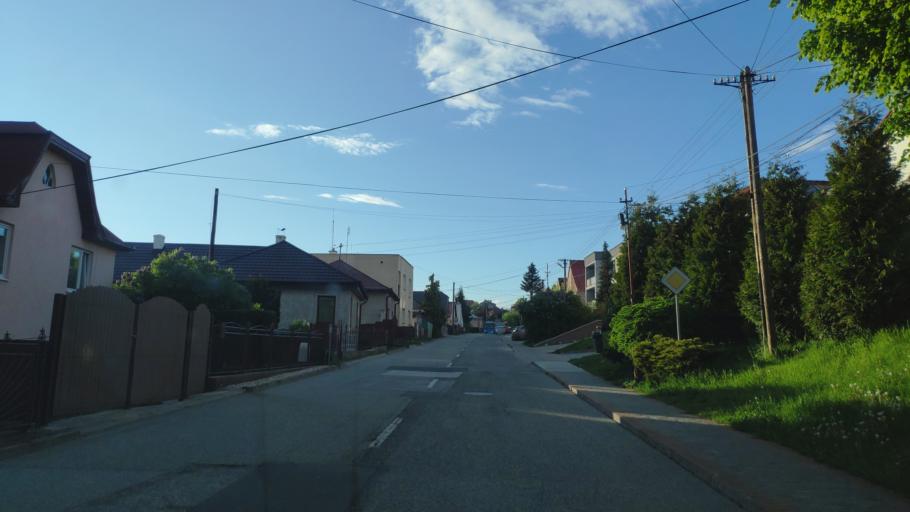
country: SK
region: Kosicky
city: Kosice
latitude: 48.7302
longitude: 21.2997
